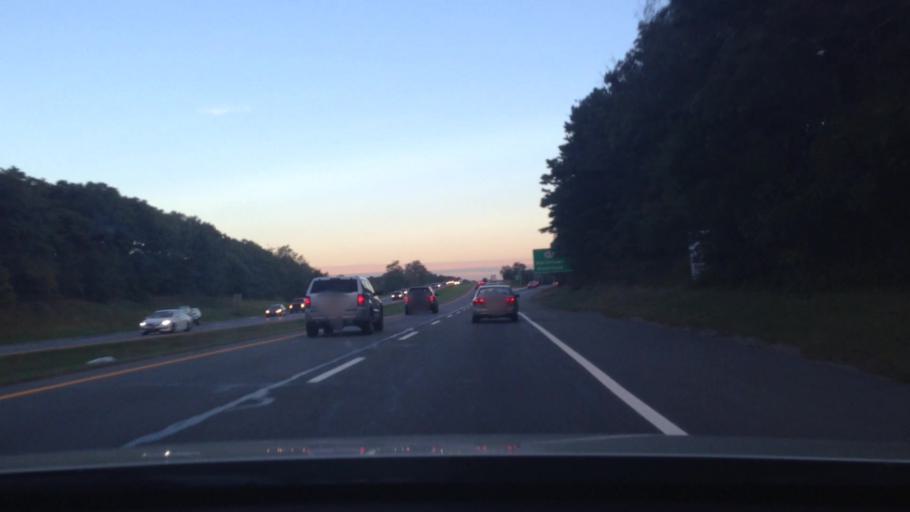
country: US
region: New York
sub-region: Suffolk County
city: Centereach
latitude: 40.8561
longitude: -73.0675
